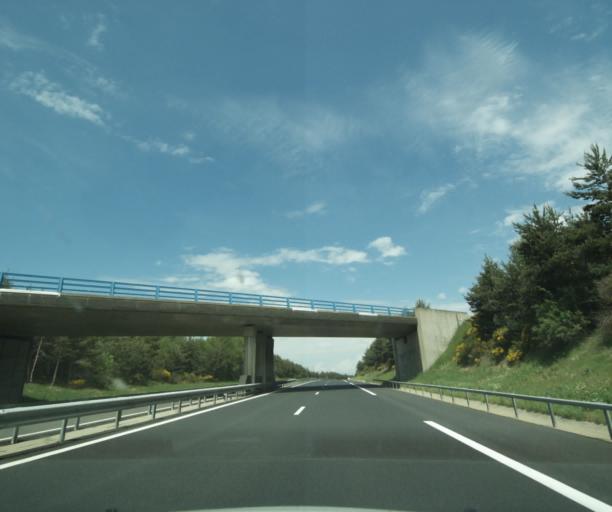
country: FR
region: Languedoc-Roussillon
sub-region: Departement de la Lozere
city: Aumont-Aubrac
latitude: 44.6734
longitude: 3.2600
